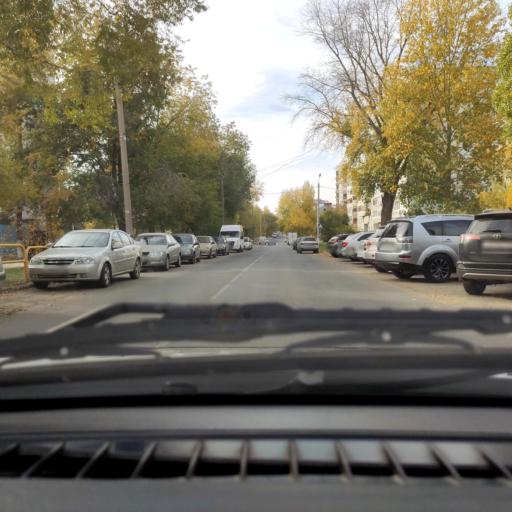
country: RU
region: Samara
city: Zhigulevsk
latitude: 53.4764
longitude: 49.4803
